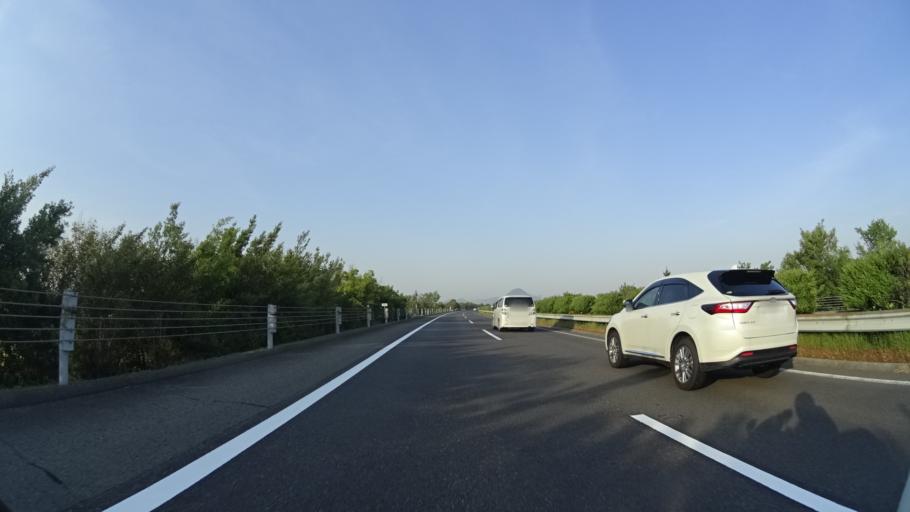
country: JP
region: Kagawa
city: Tadotsu
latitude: 34.2356
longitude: 133.7524
